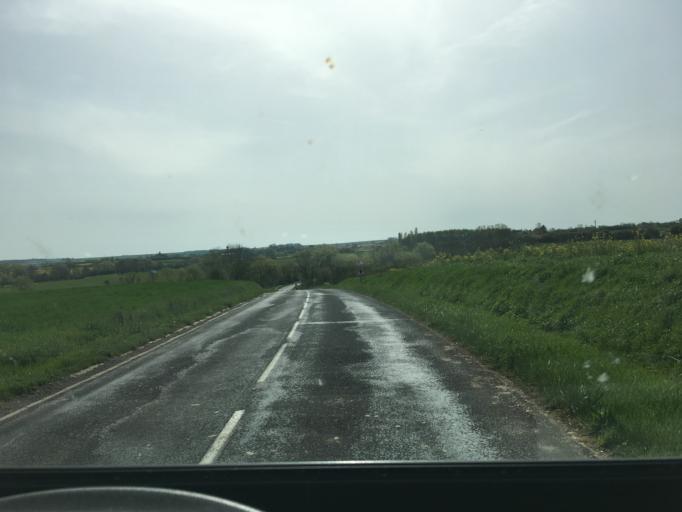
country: FR
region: Lorraine
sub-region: Departement de Meurthe-et-Moselle
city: Fleville-devant-Nancy
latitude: 48.6222
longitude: 6.2252
